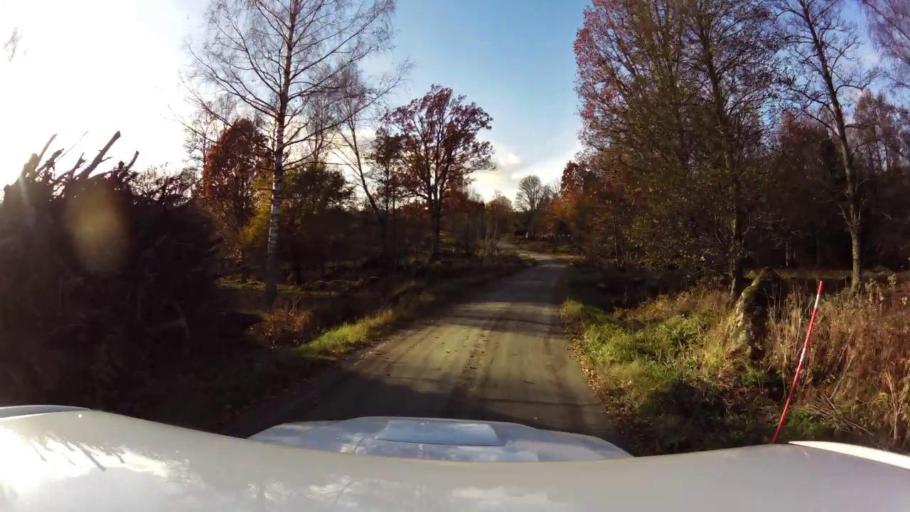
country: SE
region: OEstergoetland
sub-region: Linkopings Kommun
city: Vikingstad
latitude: 58.2198
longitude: 15.4501
